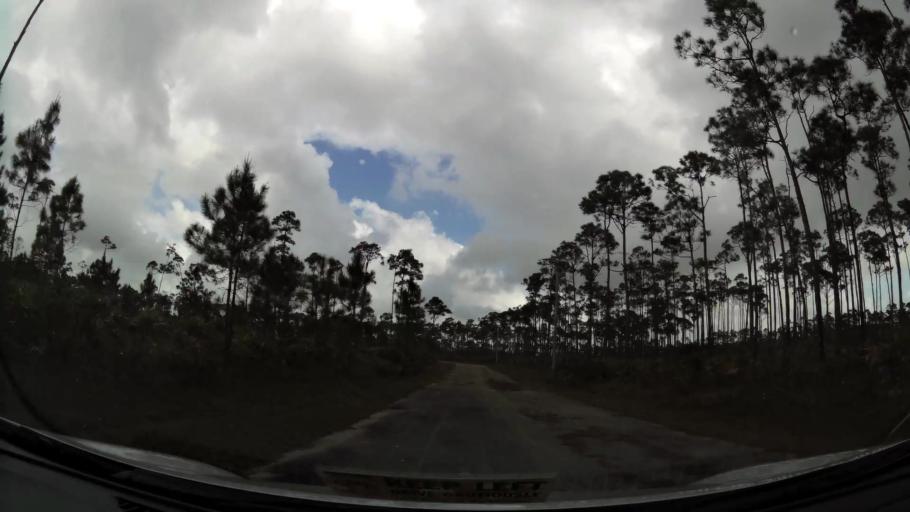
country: BS
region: Freeport
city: Lucaya
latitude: 26.5593
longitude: -78.5769
